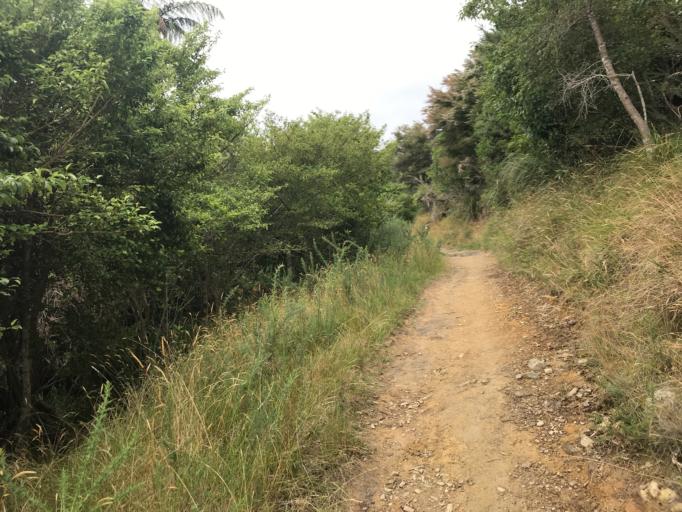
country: NZ
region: Marlborough
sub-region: Marlborough District
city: Picton
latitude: -41.2305
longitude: 173.9584
